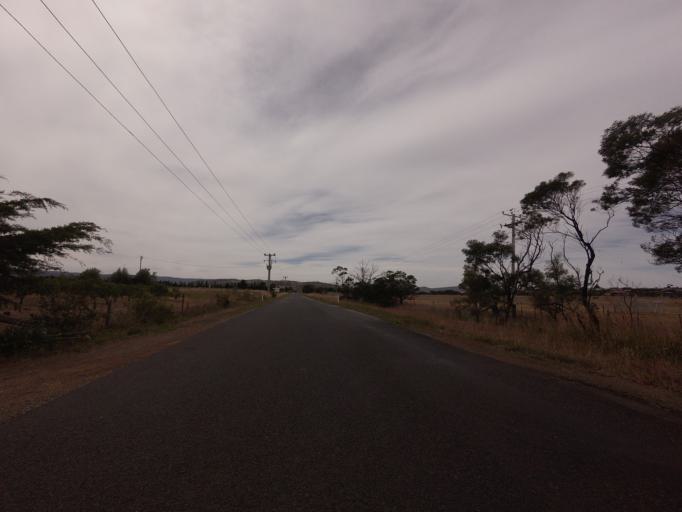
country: AU
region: Tasmania
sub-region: Sorell
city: Sorell
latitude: -42.7808
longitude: 147.5174
